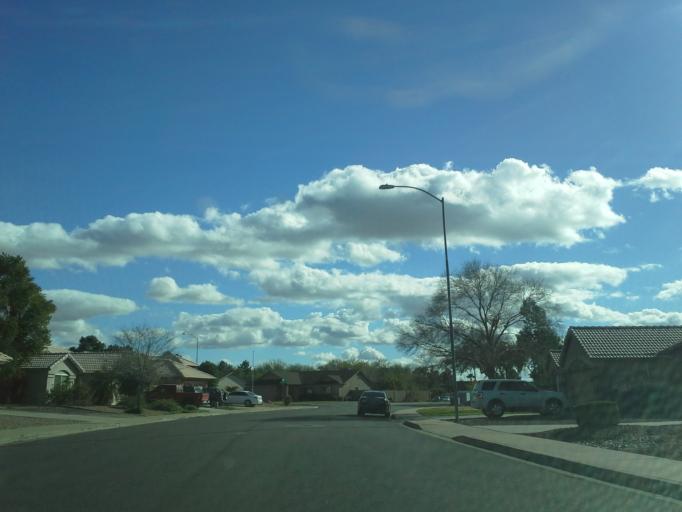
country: US
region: Arizona
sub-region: Maricopa County
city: Gilbert
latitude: 33.3961
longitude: -111.7146
